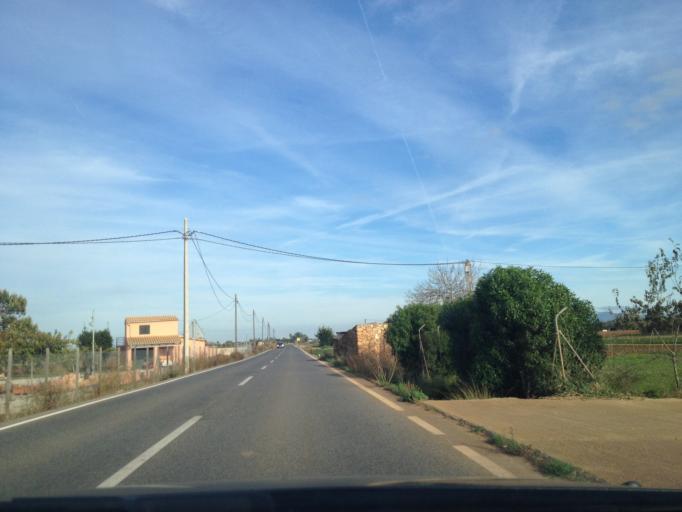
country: ES
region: Balearic Islands
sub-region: Illes Balears
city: Muro
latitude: 39.7632
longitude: 3.0724
